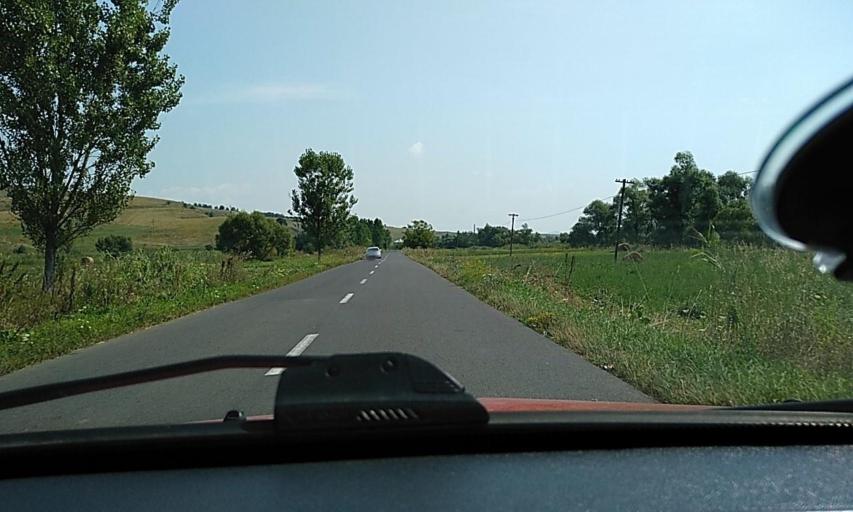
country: RO
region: Brasov
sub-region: Oras Rupea
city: Rupea
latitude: 46.0161
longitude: 25.1717
